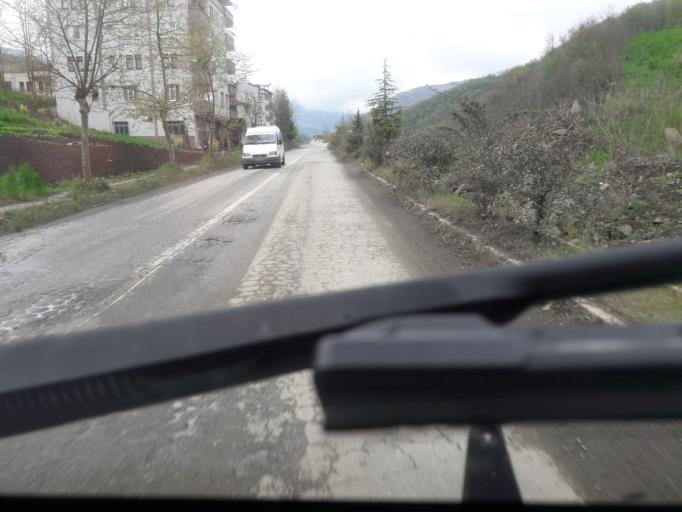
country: TR
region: Trabzon
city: Duzkoy
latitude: 40.9273
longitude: 39.4936
